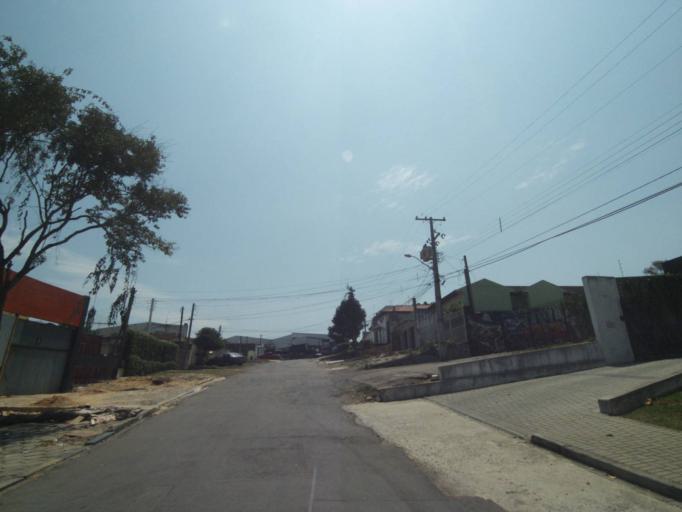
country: BR
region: Parana
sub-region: Curitiba
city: Curitiba
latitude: -25.4795
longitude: -49.3128
